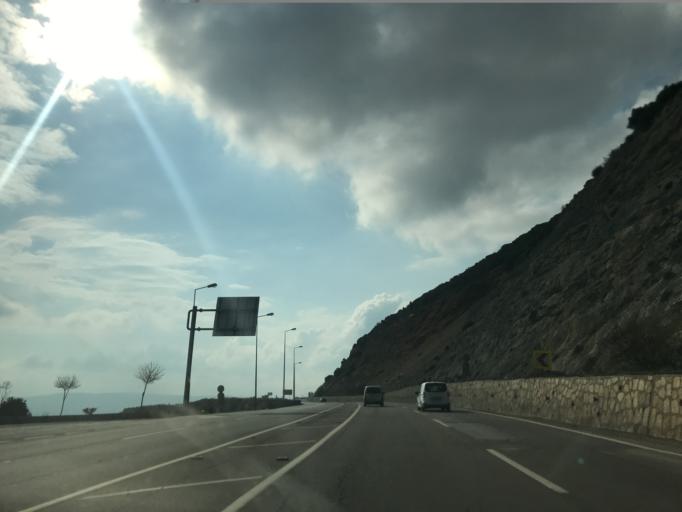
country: TR
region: Hatay
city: Belen
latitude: 36.4769
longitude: 36.2551
